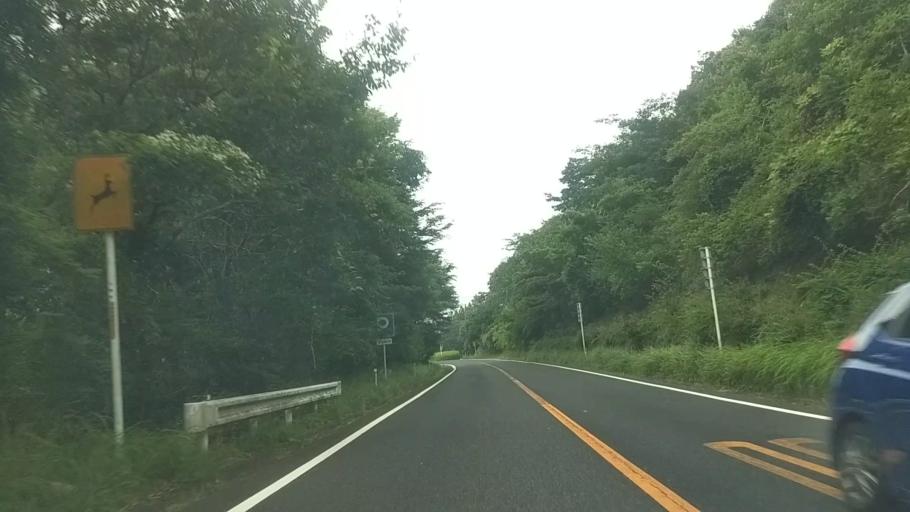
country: JP
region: Chiba
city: Kawaguchi
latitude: 35.2279
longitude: 140.0316
